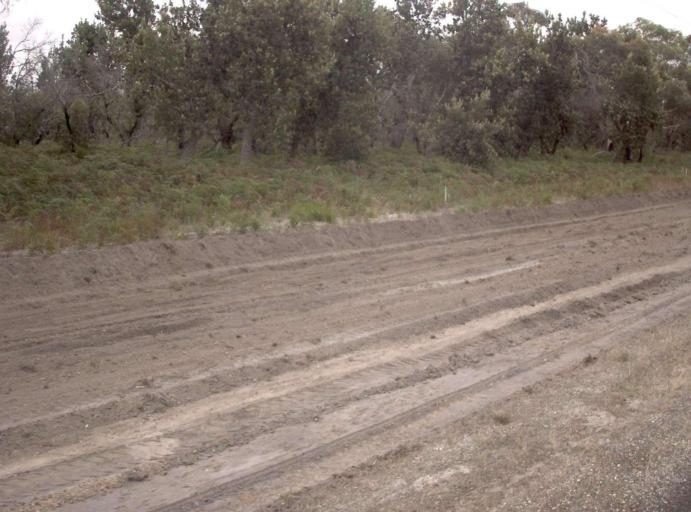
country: AU
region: Victoria
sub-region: East Gippsland
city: Bairnsdale
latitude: -38.0729
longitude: 147.5452
